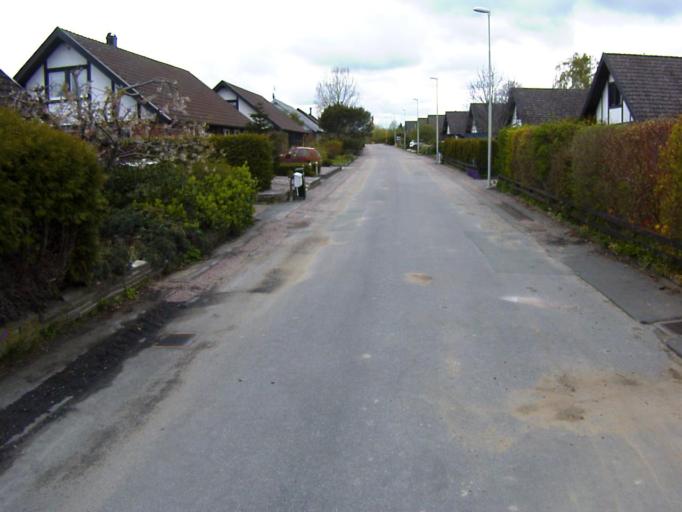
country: SE
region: Skane
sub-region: Kristianstads Kommun
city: Kristianstad
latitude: 56.0470
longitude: 14.1886
